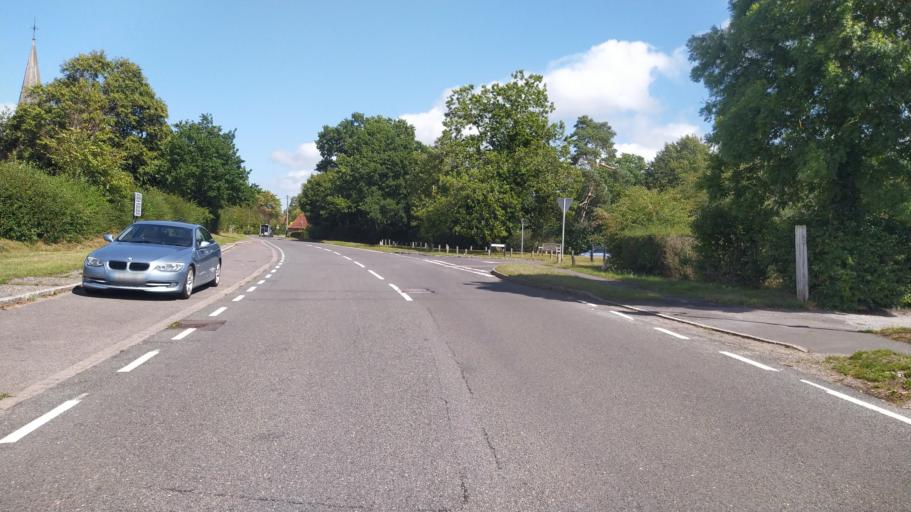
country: GB
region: England
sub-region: Hampshire
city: Liss
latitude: 51.0669
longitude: -0.8978
